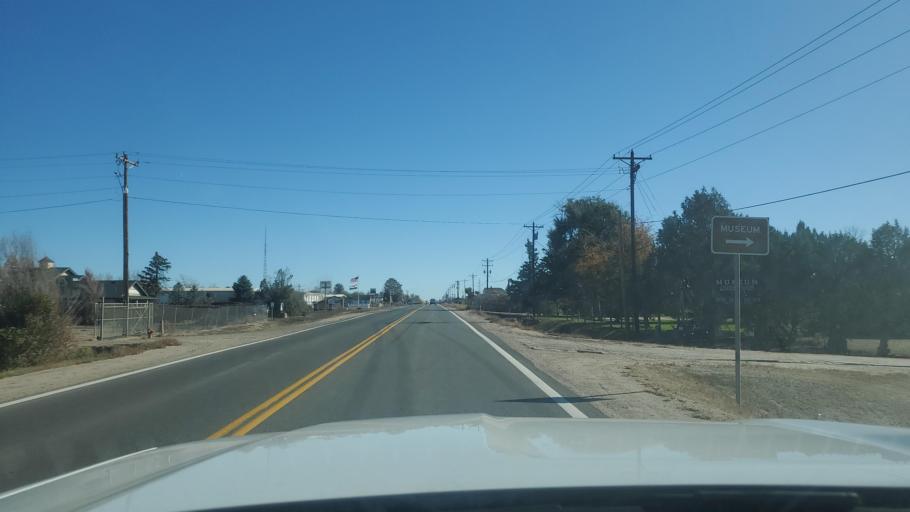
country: US
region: Colorado
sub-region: Adams County
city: Strasburg
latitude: 39.7383
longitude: -104.3314
